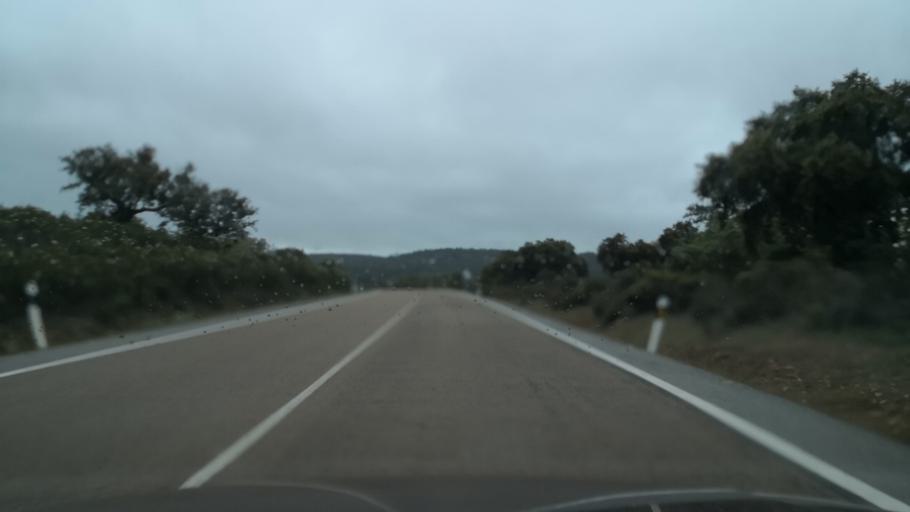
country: ES
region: Extremadura
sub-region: Provincia de Caceres
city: Malpartida de Caceres
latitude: 39.2917
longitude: -6.5220
